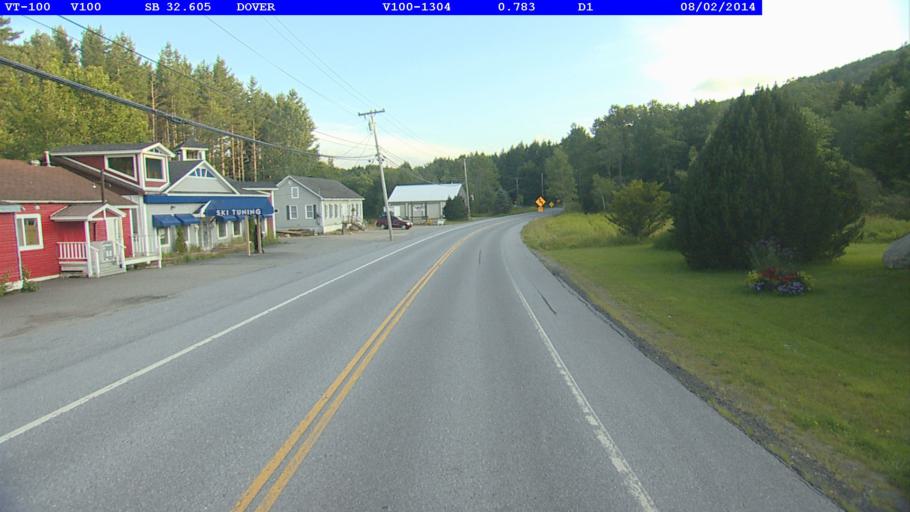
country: US
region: Vermont
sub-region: Windham County
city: Dover
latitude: 42.9350
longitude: -72.8487
